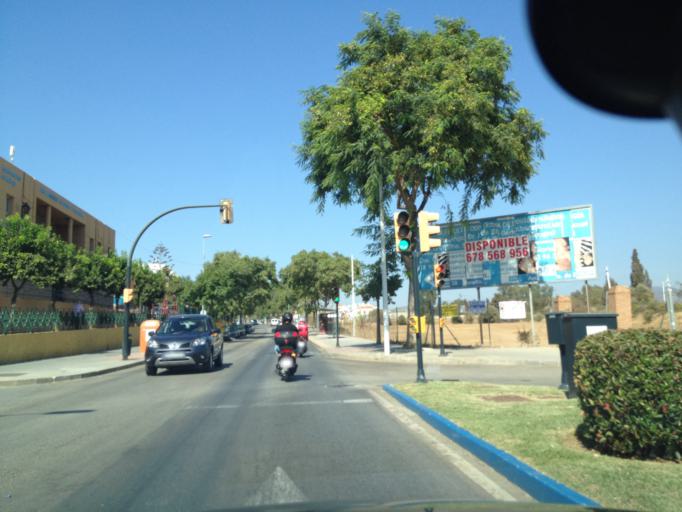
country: ES
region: Andalusia
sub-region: Provincia de Malaga
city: Alhaurin de la Torre
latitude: 36.7279
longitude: -4.5446
